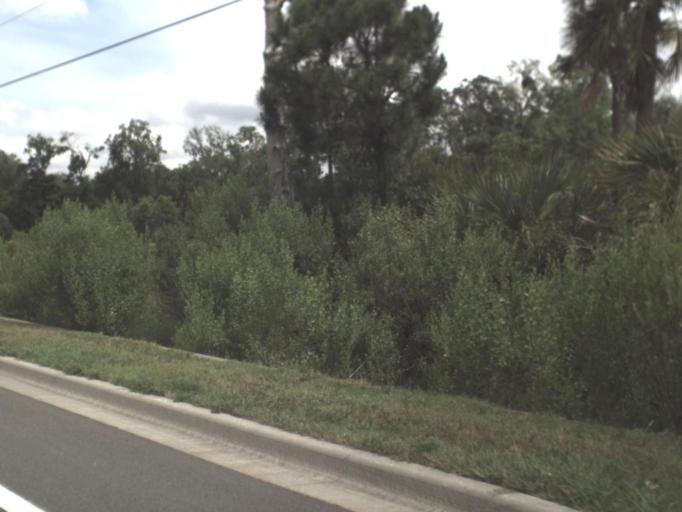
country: US
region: Florida
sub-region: Duval County
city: Jacksonville
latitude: 30.4148
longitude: -81.5911
